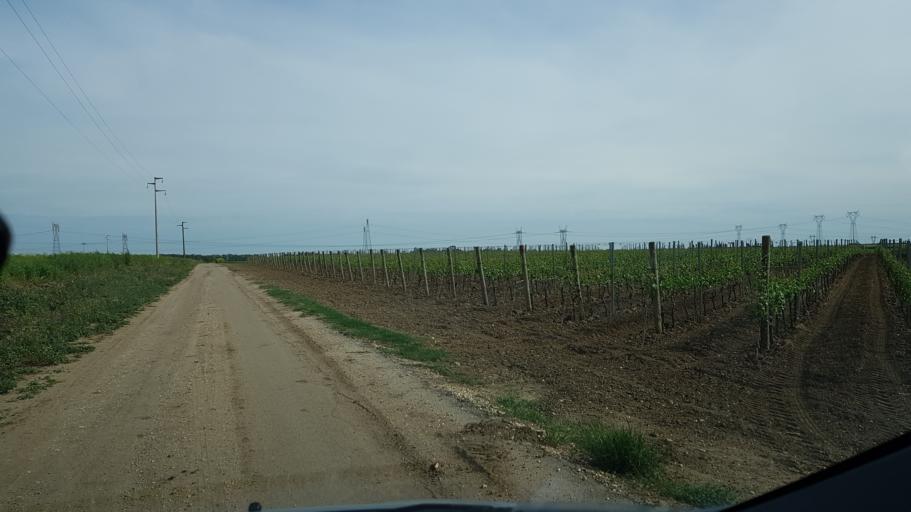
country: IT
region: Apulia
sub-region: Provincia di Brindisi
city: Tuturano
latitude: 40.5588
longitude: 17.9224
